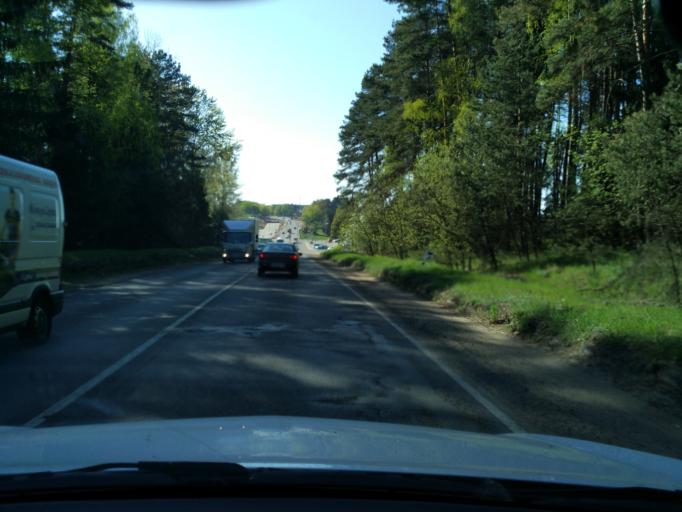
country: BY
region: Minsk
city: Borovlyany
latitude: 53.9634
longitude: 27.6769
